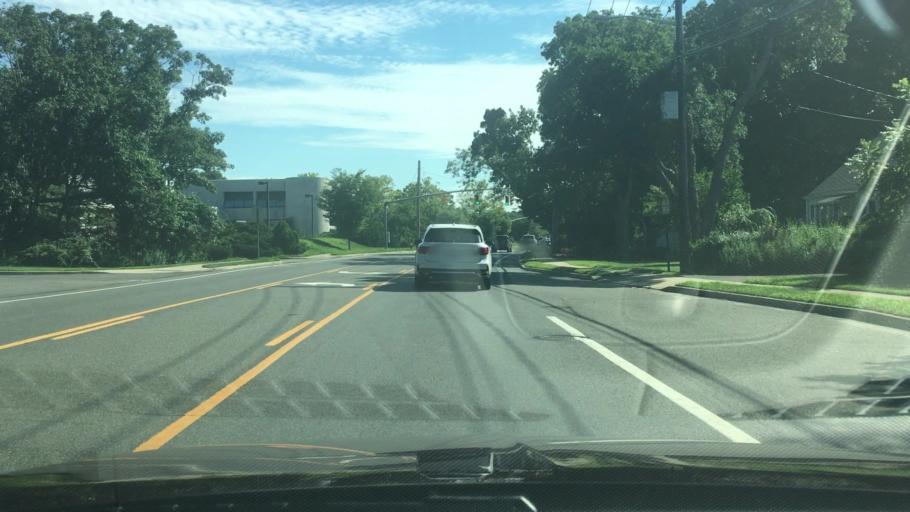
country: US
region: New York
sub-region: Suffolk County
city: Melville
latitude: 40.7756
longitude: -73.4257
